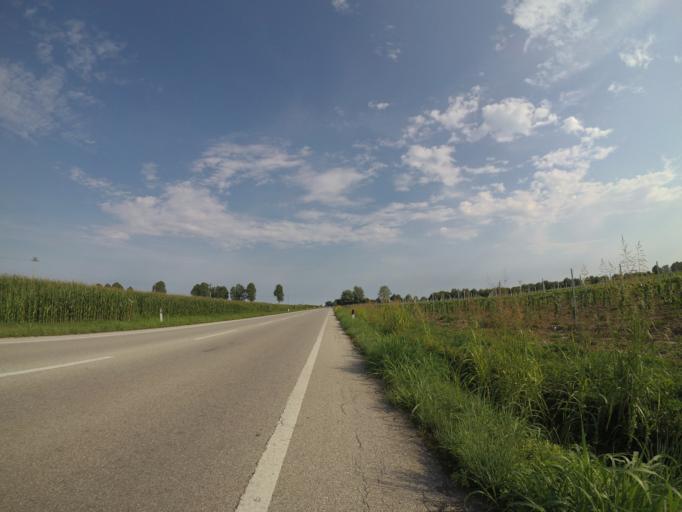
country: IT
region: Friuli Venezia Giulia
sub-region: Provincia di Udine
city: Codroipo
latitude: 45.9320
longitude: 12.9806
